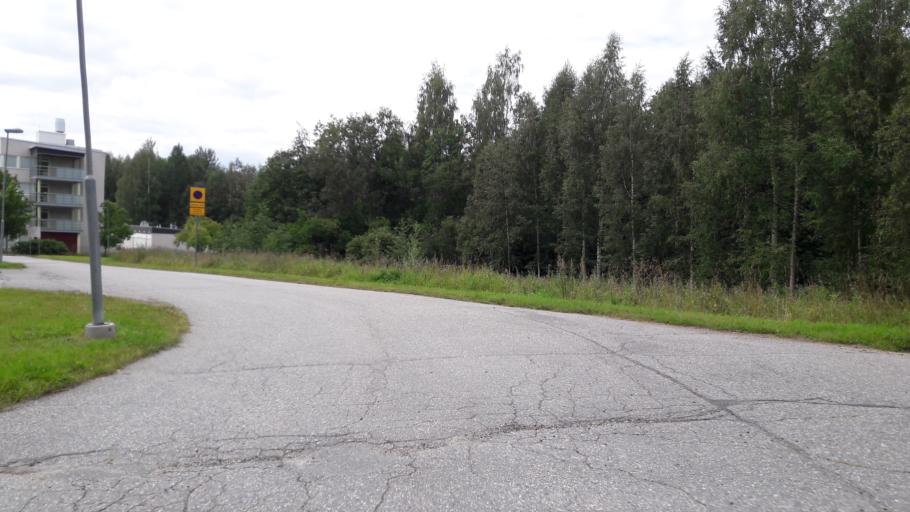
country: FI
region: North Karelia
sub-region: Joensuu
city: Joensuu
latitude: 62.5749
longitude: 29.7975
